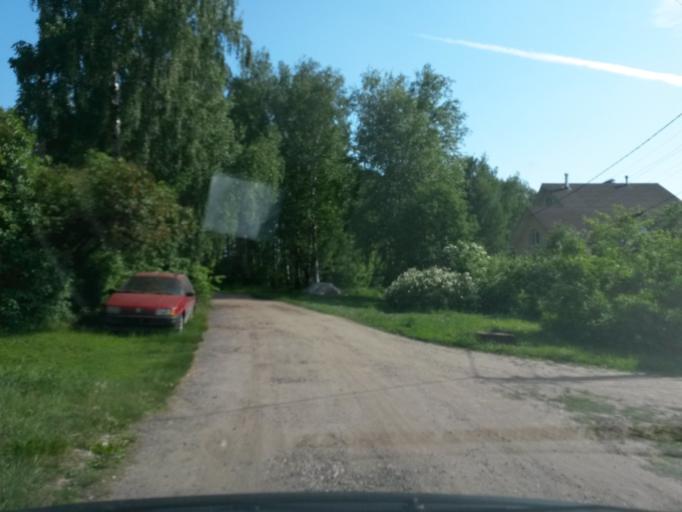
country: RU
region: Jaroslavl
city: Yaroslavl
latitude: 57.6411
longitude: 39.7883
